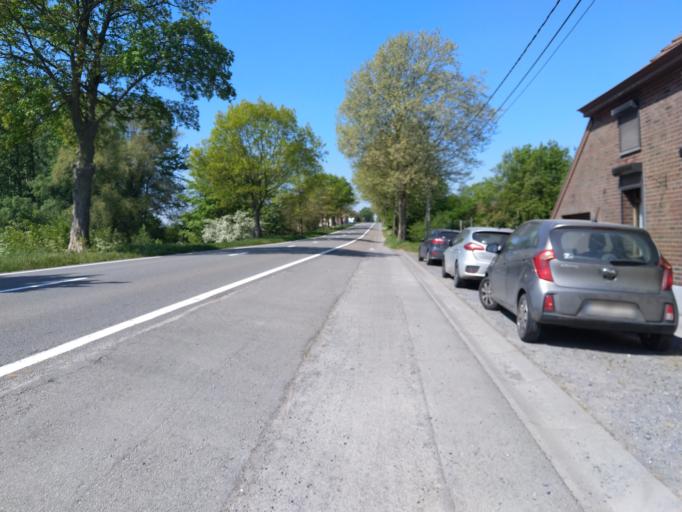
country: BE
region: Wallonia
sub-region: Province du Hainaut
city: Soignies
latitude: 50.6074
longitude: 4.0127
